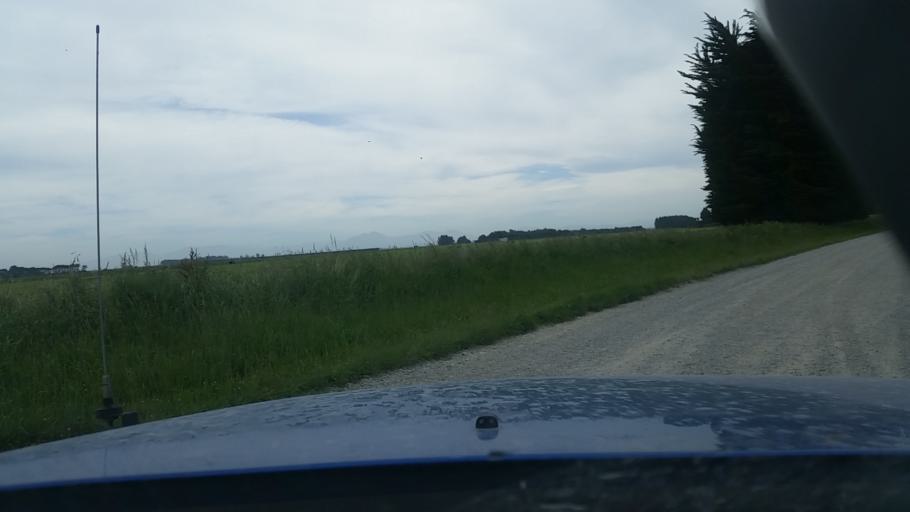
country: NZ
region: Canterbury
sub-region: Ashburton District
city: Tinwald
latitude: -44.0640
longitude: 171.7546
